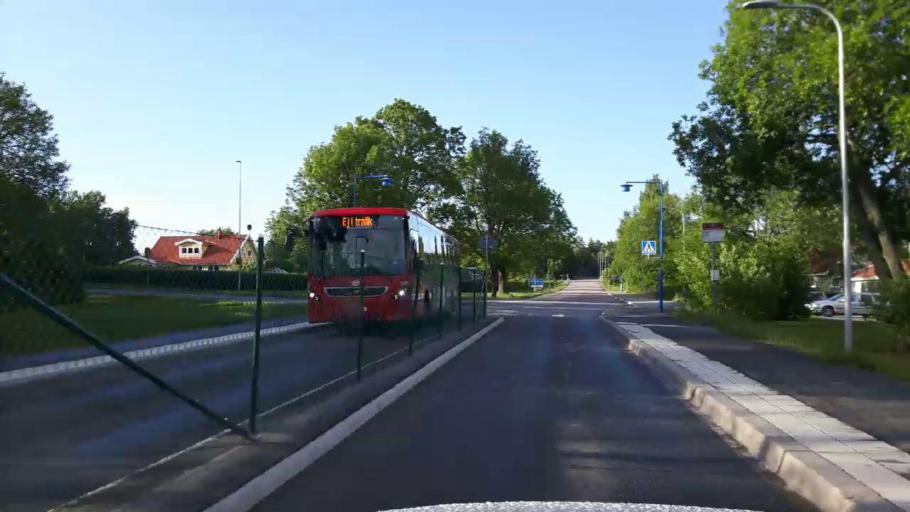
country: SE
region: Stockholm
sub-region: Upplands-Bro Kommun
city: Bro
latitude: 59.5178
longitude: 17.6572
